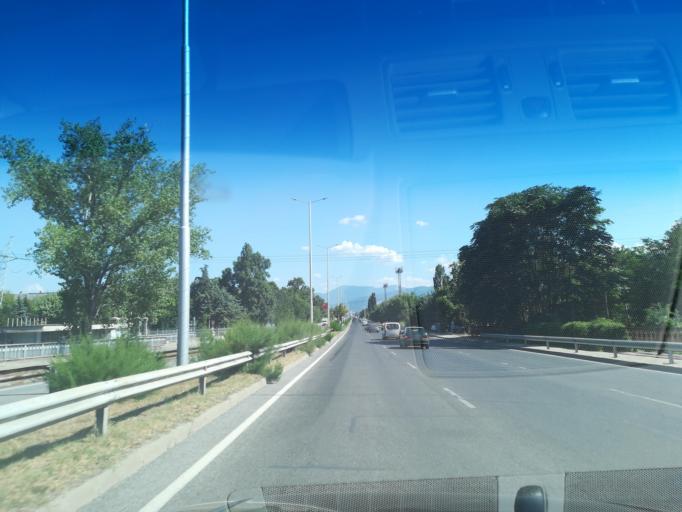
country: BG
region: Plovdiv
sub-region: Obshtina Plovdiv
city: Plovdiv
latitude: 42.1135
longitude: 24.7791
